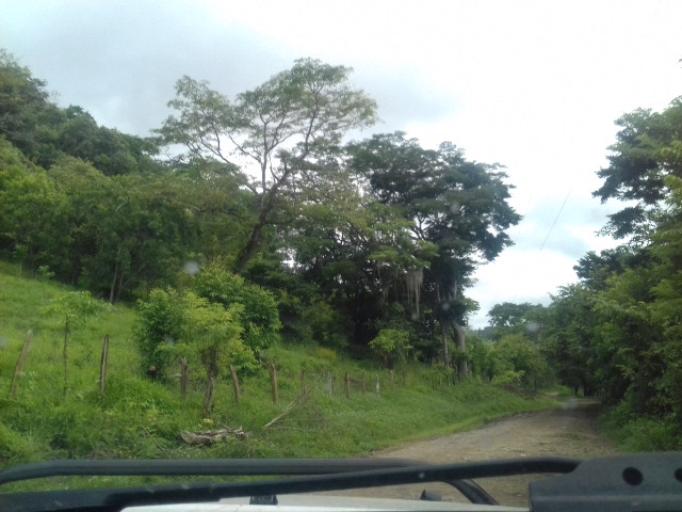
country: NI
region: Matagalpa
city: Matiguas
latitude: 12.8642
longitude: -85.3877
